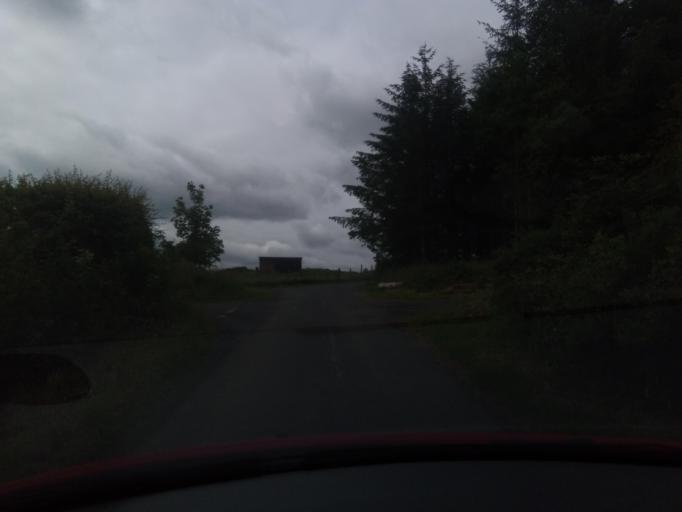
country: GB
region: Scotland
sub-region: The Scottish Borders
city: Hawick
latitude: 55.4412
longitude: -2.8140
